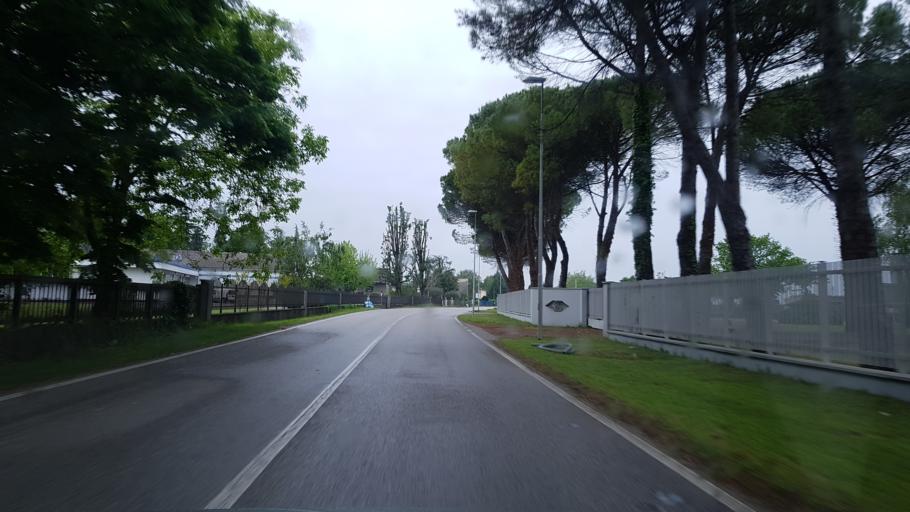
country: IT
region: Friuli Venezia Giulia
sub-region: Provincia di Udine
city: San Giovanni al Natisone
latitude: 45.9833
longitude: 13.4166
